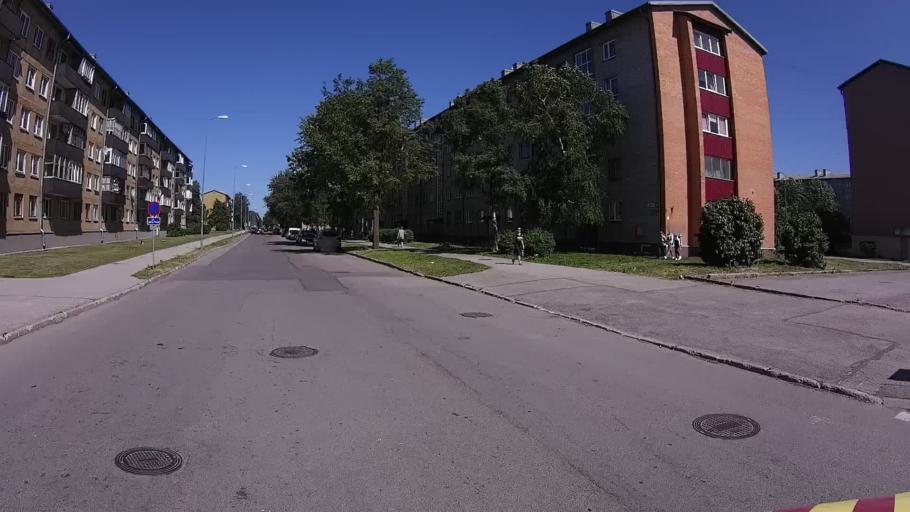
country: EE
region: Ida-Virumaa
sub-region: Kohtla-Jaerve linn
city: Kohtla-Jarve
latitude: 59.4063
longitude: 27.2834
